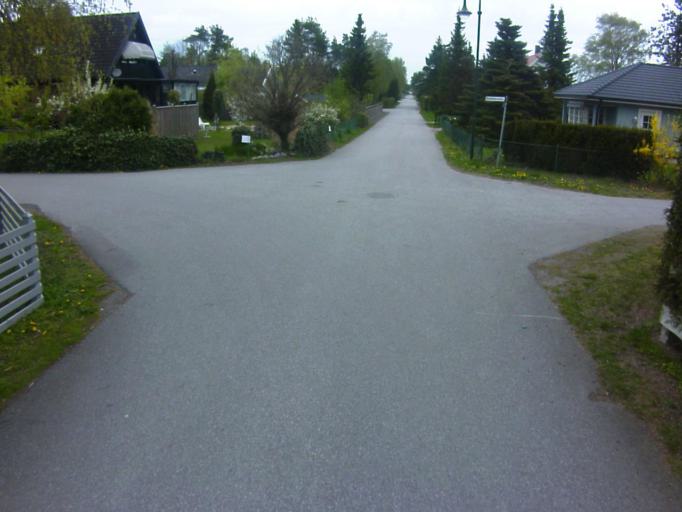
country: SE
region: Skane
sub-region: Kavlinge Kommun
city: Loddekopinge
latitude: 55.7489
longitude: 12.9937
